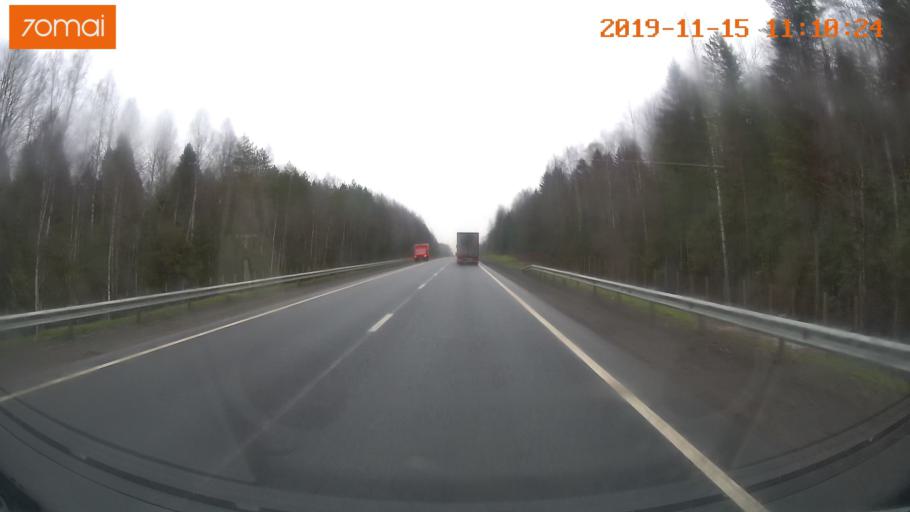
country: RU
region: Vologda
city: Chebsara
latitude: 59.1209
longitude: 39.1193
